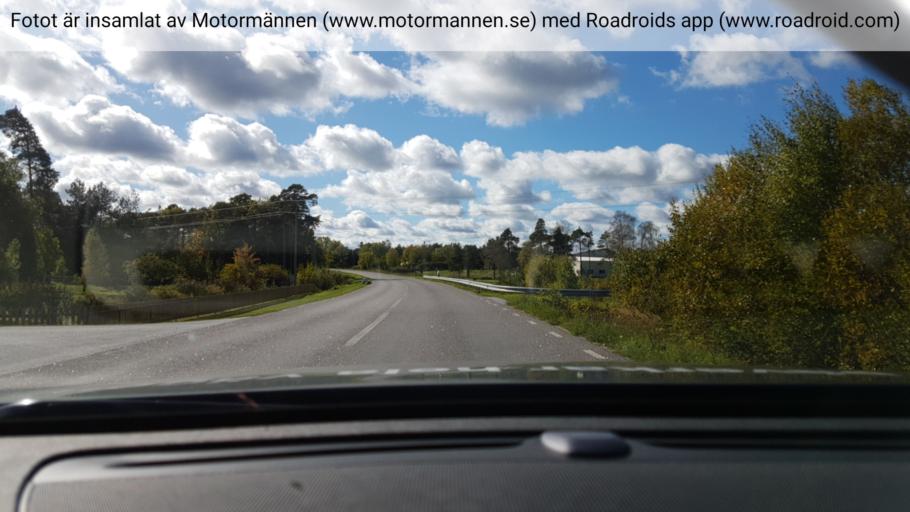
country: SE
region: Gotland
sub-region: Gotland
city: Slite
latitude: 57.4446
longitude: 18.7054
